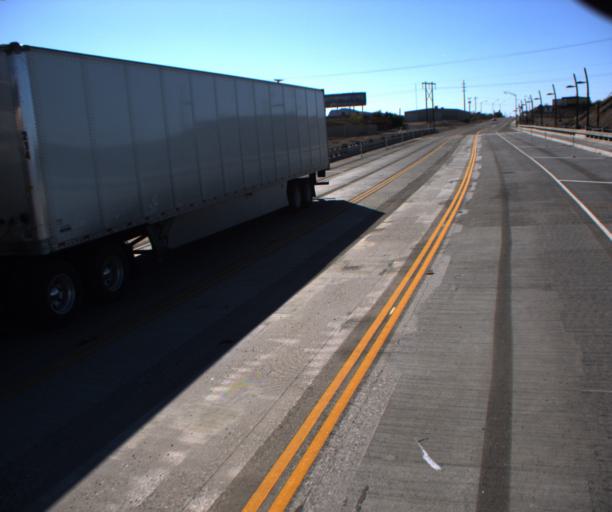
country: US
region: Arizona
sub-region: La Paz County
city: Parker
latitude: 34.1594
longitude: -114.2989
